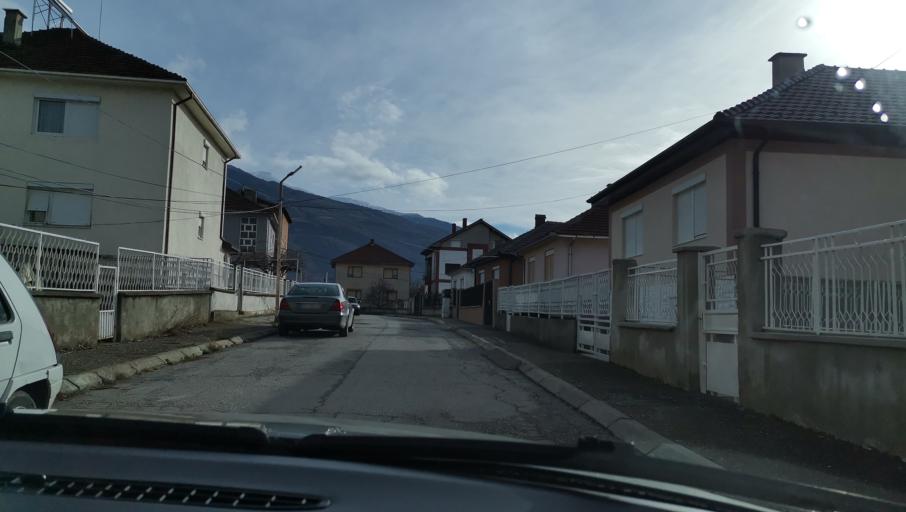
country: MK
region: Debar
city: Debar
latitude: 41.5163
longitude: 20.5314
